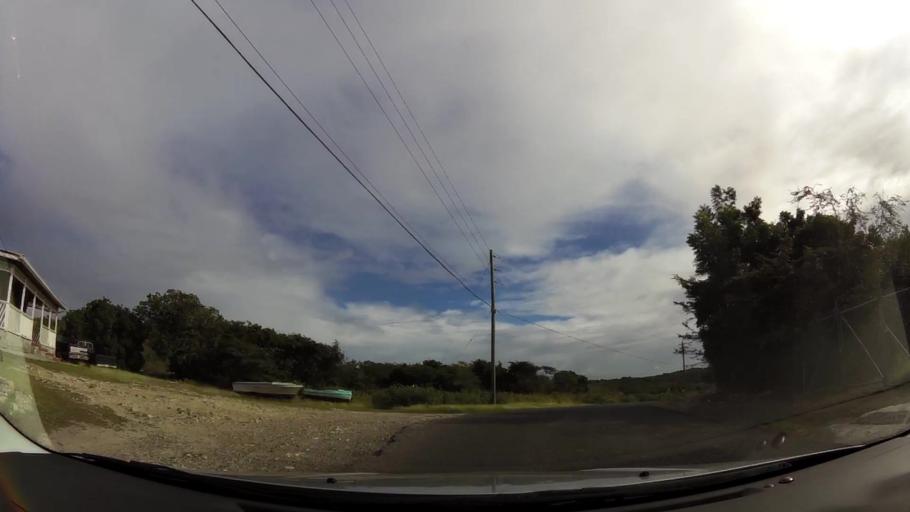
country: AG
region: Saint Peter
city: Parham
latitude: 17.0908
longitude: -61.7001
